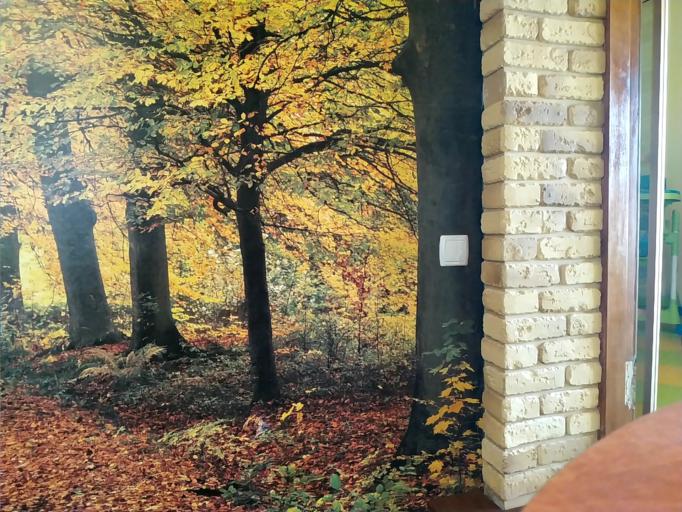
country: RU
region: Tverskaya
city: Rameshki
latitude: 57.5317
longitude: 35.9499
